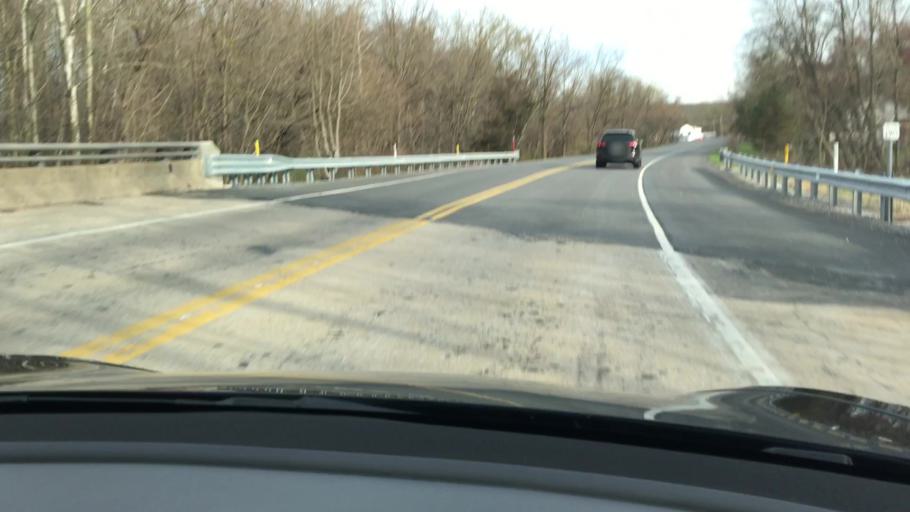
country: US
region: Pennsylvania
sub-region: York County
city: Valley Green
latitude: 40.1382
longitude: -76.8668
